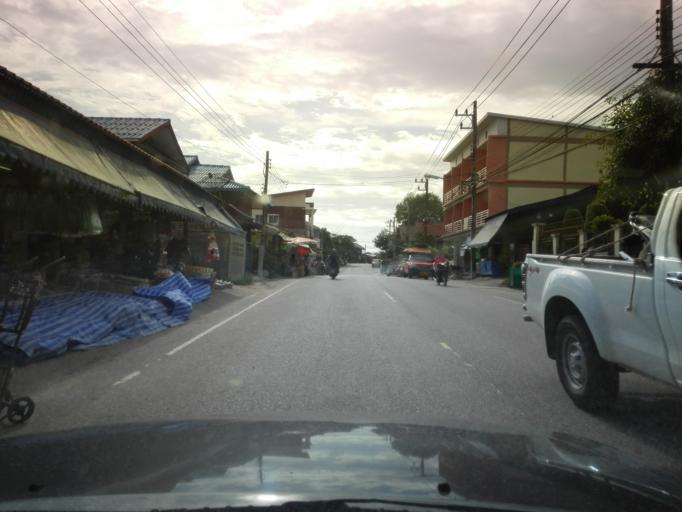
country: TH
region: Tak
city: Mae Ramat
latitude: 16.9796
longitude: 98.5228
